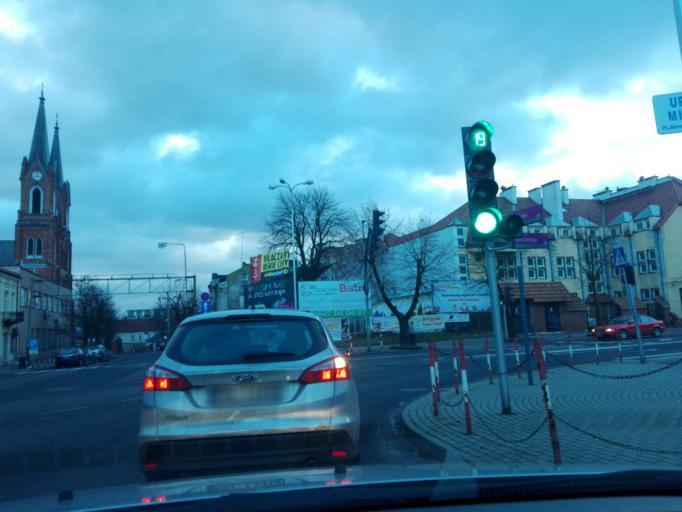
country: PL
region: Lodz Voivodeship
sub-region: Powiat kutnowski
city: Kutno
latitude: 52.2320
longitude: 19.3630
